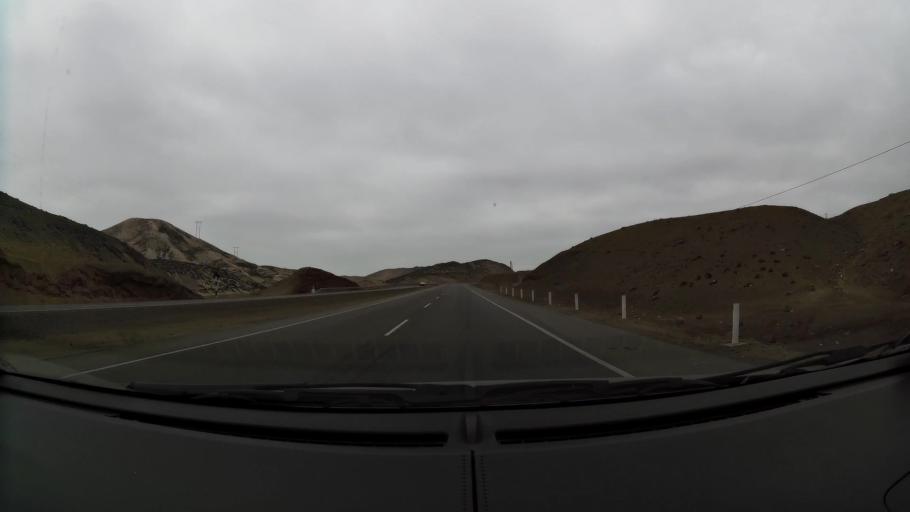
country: PE
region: Lima
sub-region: Barranca
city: Paramonga
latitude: -10.4738
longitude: -77.9153
